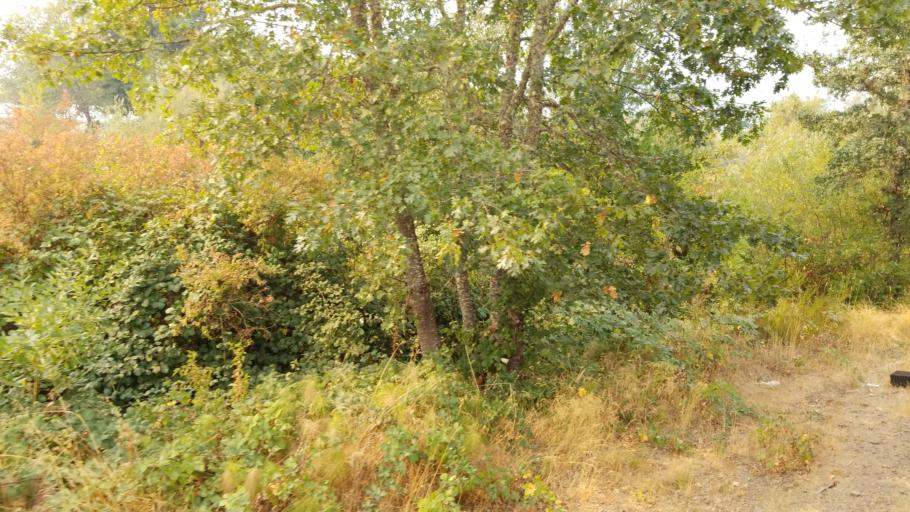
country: US
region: California
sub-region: Mendocino County
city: Willits
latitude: 39.4019
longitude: -123.3551
